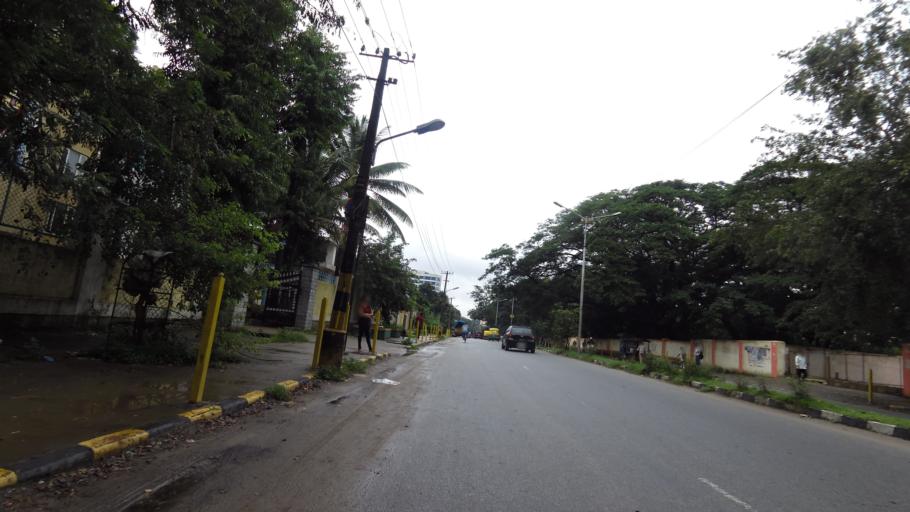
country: IN
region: Karnataka
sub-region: Bangalore Urban
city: Bangalore
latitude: 12.9851
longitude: 77.6453
